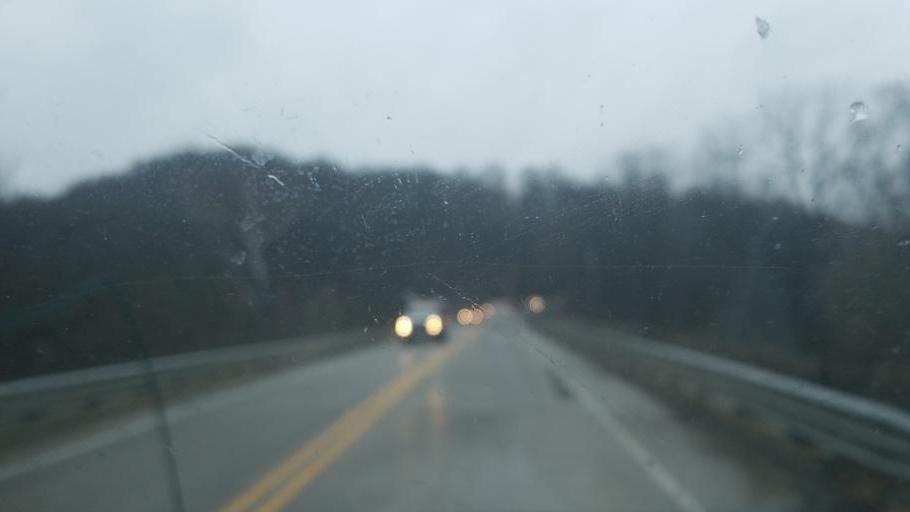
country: US
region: Indiana
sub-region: Brown County
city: Nashville
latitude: 39.2020
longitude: -86.2471
